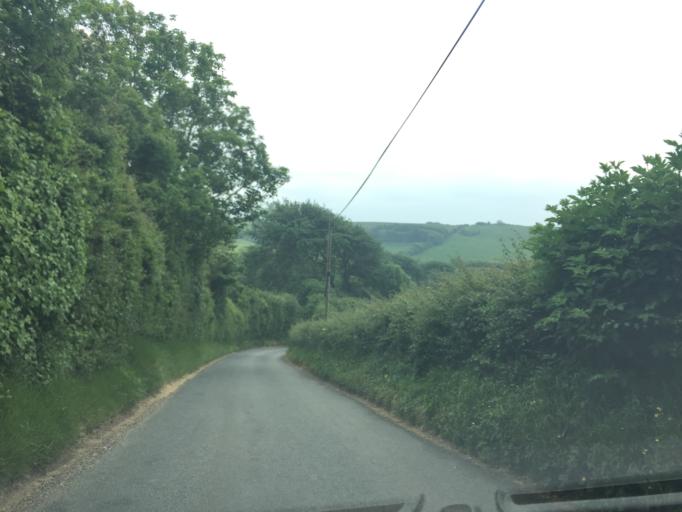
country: GB
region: England
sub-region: Dorset
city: Overcombe
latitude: 50.6496
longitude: -2.3688
